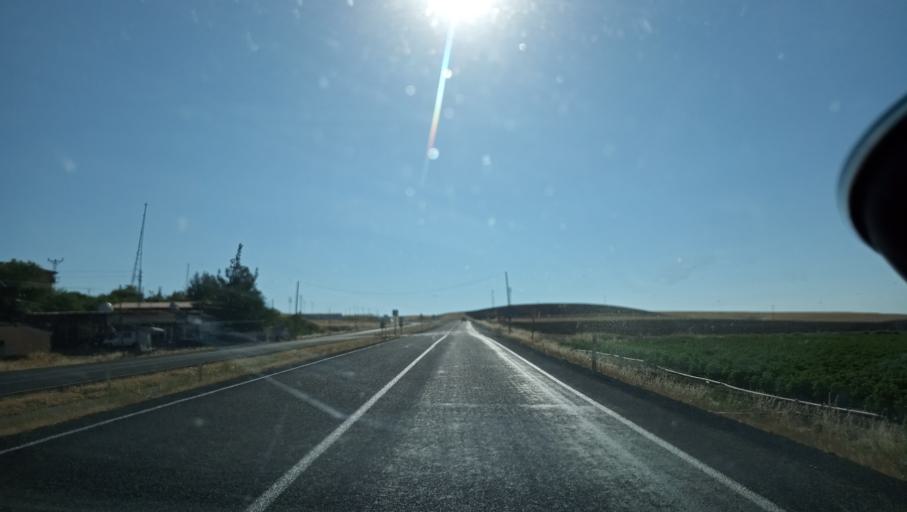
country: TR
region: Diyarbakir
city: Sur
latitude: 37.9913
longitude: 40.3897
